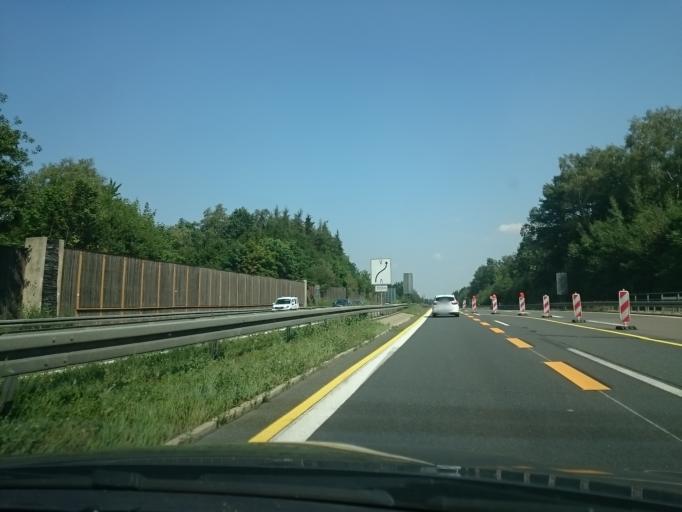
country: DE
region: Saxony
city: Hirschfeld
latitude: 50.6407
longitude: 12.4446
